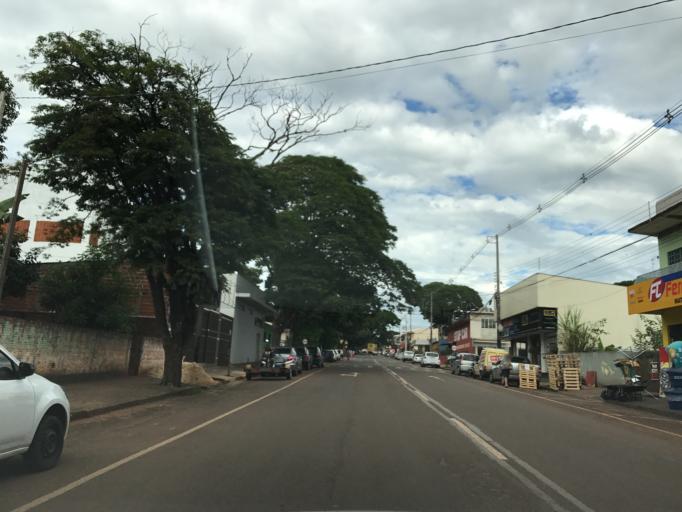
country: BR
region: Parana
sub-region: Sarandi
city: Sarandi
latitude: -23.4343
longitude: -51.8692
